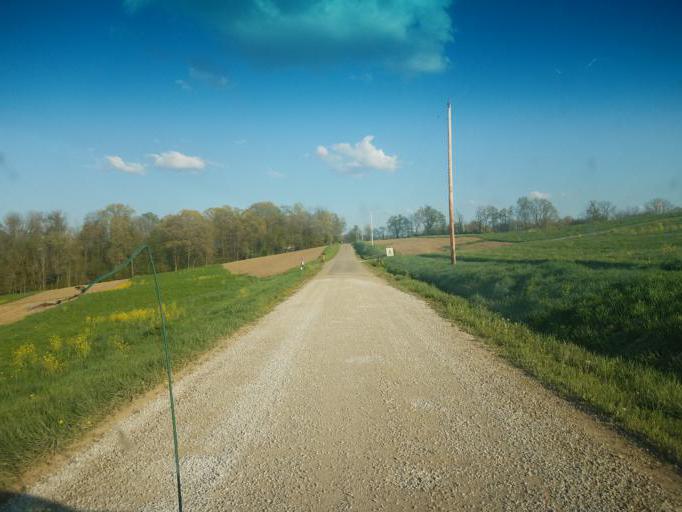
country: US
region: Ohio
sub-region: Holmes County
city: Millersburg
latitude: 40.5830
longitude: -81.9992
